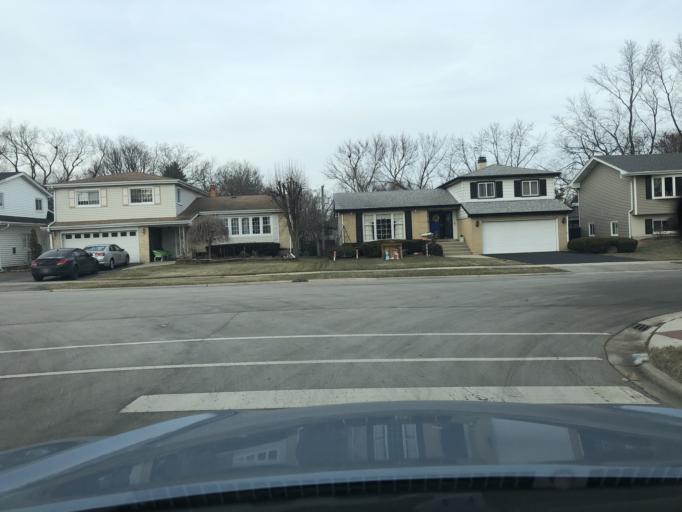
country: US
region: Illinois
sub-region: DuPage County
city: Addison
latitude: 41.9334
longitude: -88.0101
